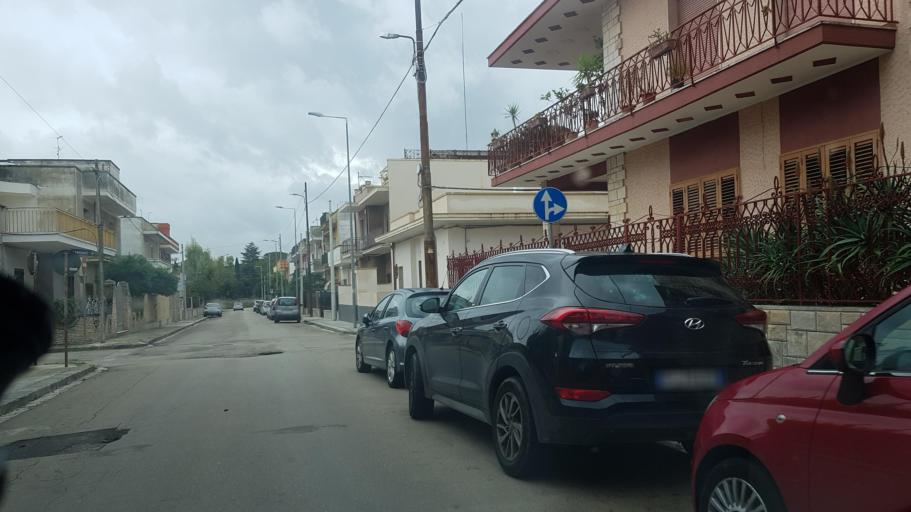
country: IT
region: Apulia
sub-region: Provincia di Lecce
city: Novoli
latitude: 40.3735
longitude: 18.0466
